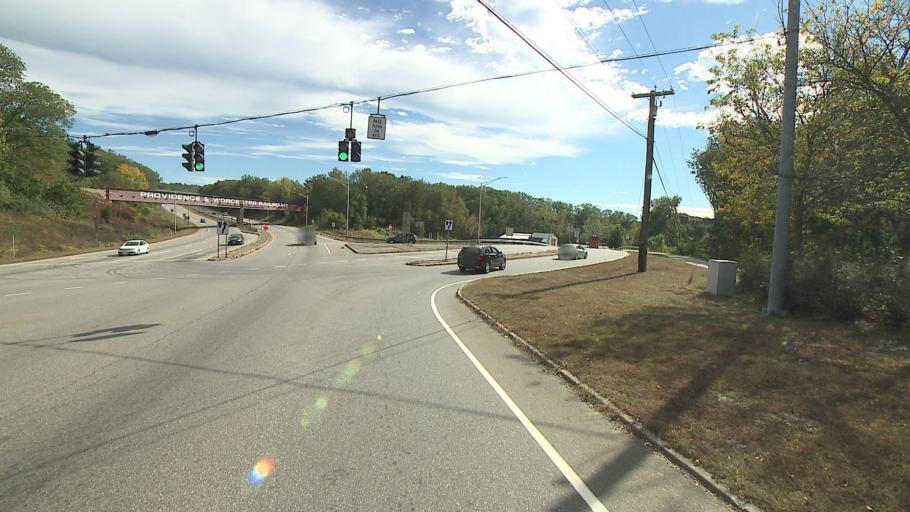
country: US
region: Connecticut
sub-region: Windham County
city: Danielson
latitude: 41.7969
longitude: -71.8848
